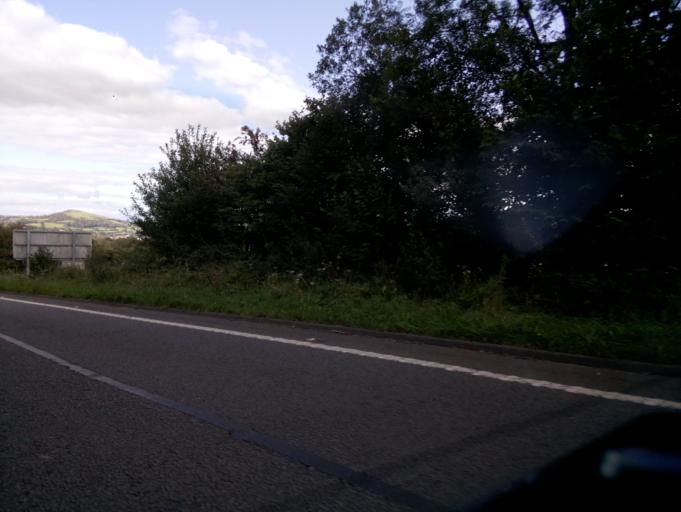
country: GB
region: England
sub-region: Devon
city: South Brent
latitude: 50.4059
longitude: -3.8511
